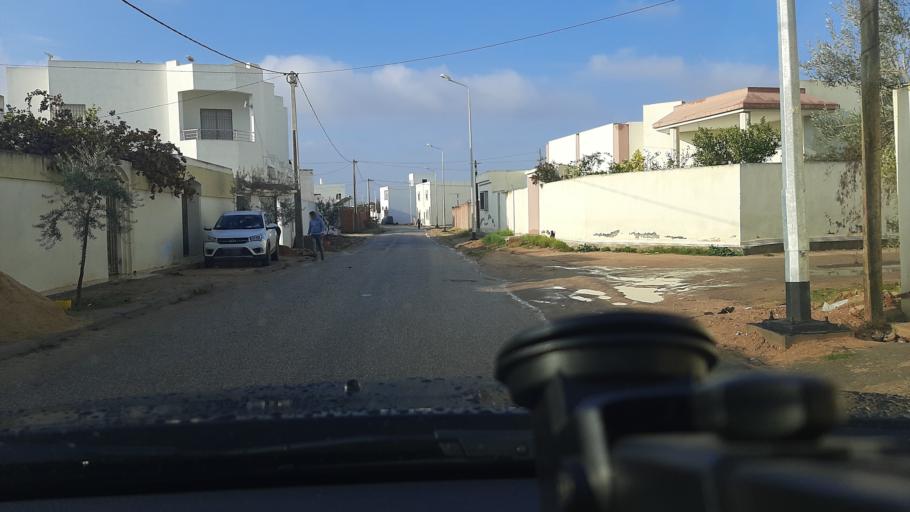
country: TN
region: Safaqis
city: Sfax
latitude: 34.7429
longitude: 10.7165
